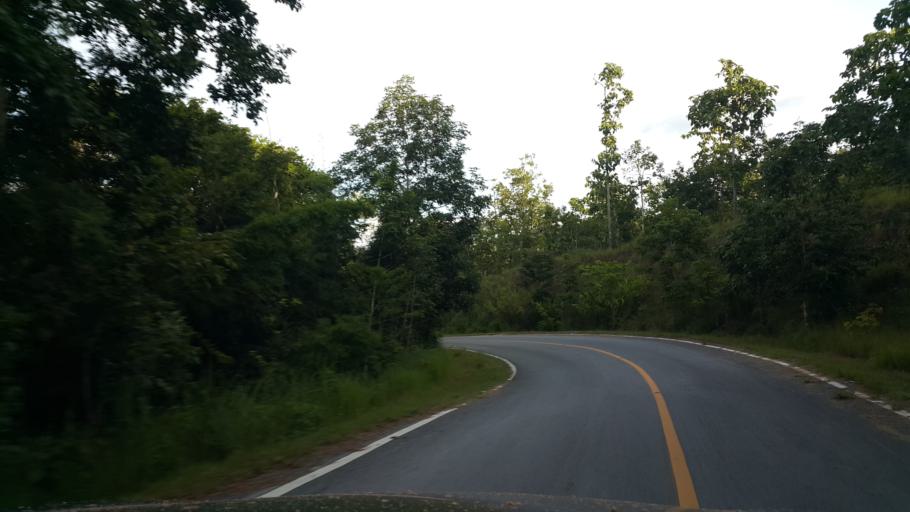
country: TH
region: Mae Hong Son
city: Mae Hi
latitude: 19.1804
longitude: 98.4034
